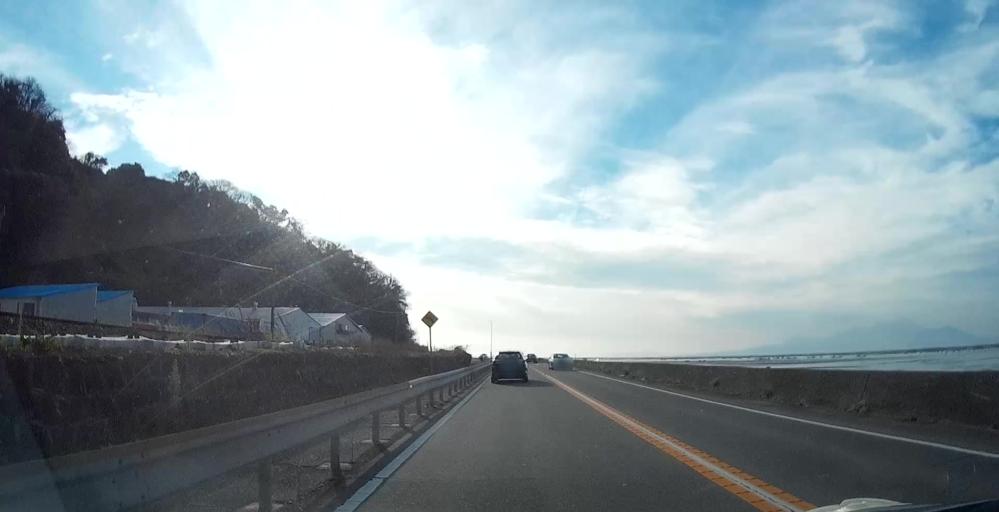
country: JP
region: Kumamoto
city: Uto
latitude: 32.6996
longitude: 130.5688
